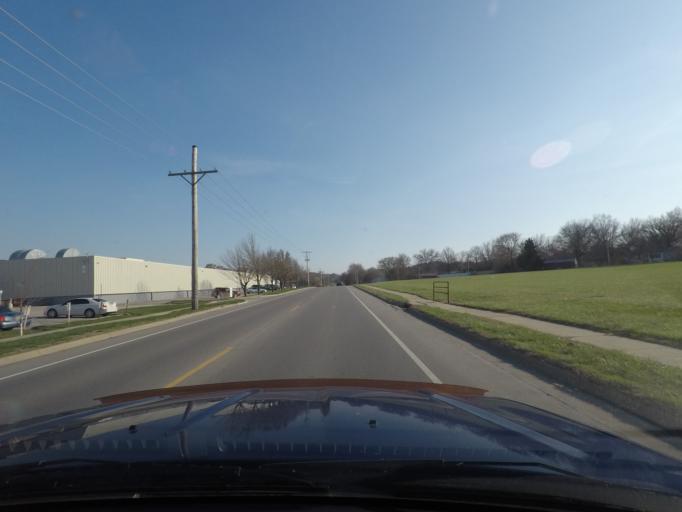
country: US
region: Kansas
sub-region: Douglas County
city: Lawrence
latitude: 38.9850
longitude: -95.2605
